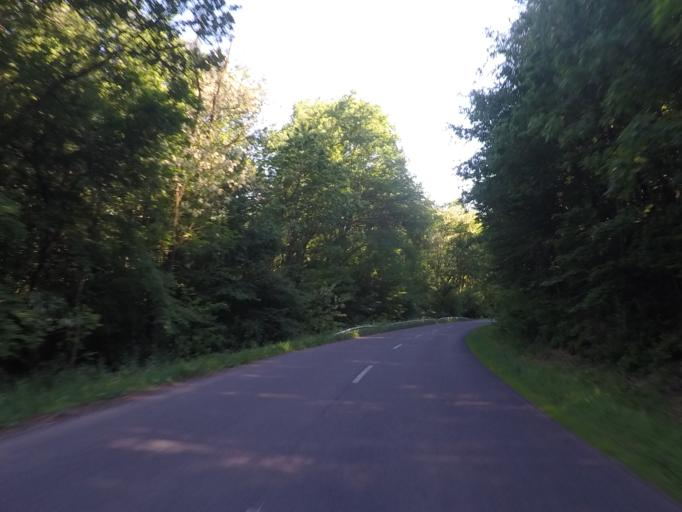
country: HU
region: Borsod-Abauj-Zemplen
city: Putnok
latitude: 48.4506
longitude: 20.4802
